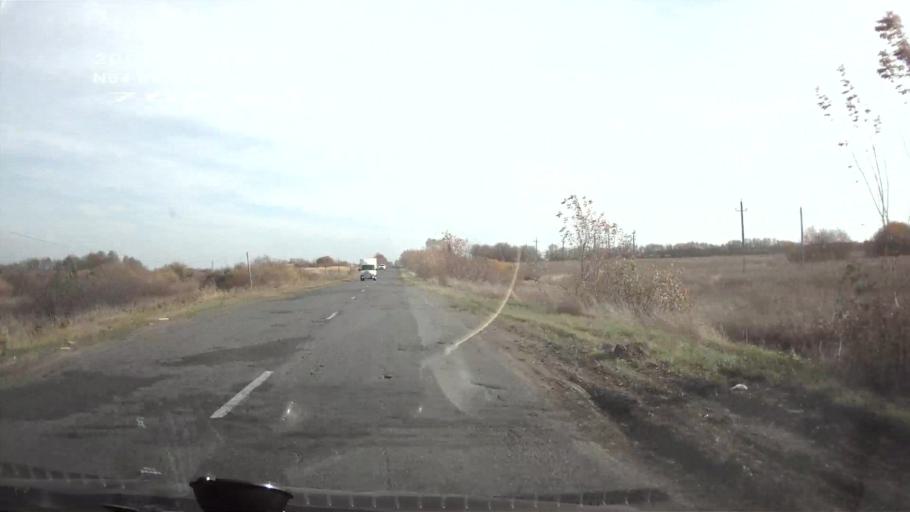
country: RU
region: Chuvashia
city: Alatyr'
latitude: 54.8455
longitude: 46.4588
